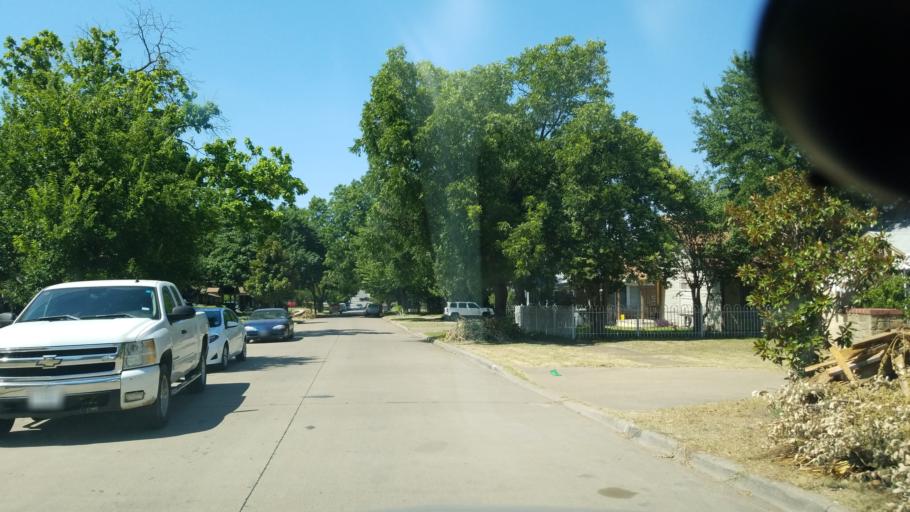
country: US
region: Texas
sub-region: Dallas County
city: Cockrell Hill
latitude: 32.7324
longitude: -96.8531
